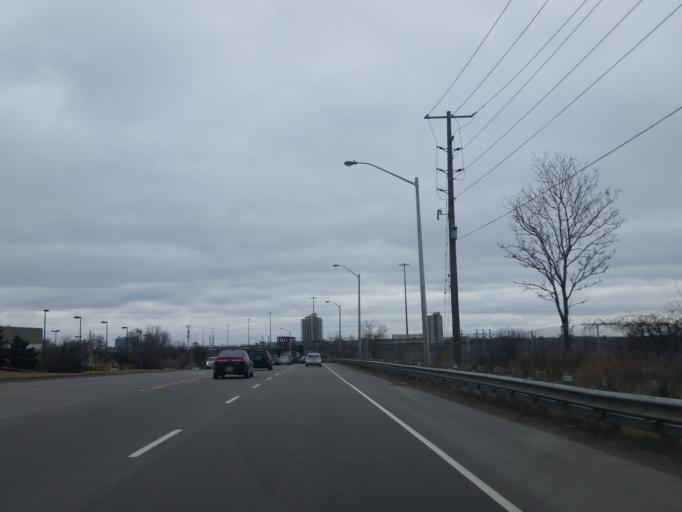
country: CA
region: Ontario
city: Ajax
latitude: 43.8240
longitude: -79.1049
